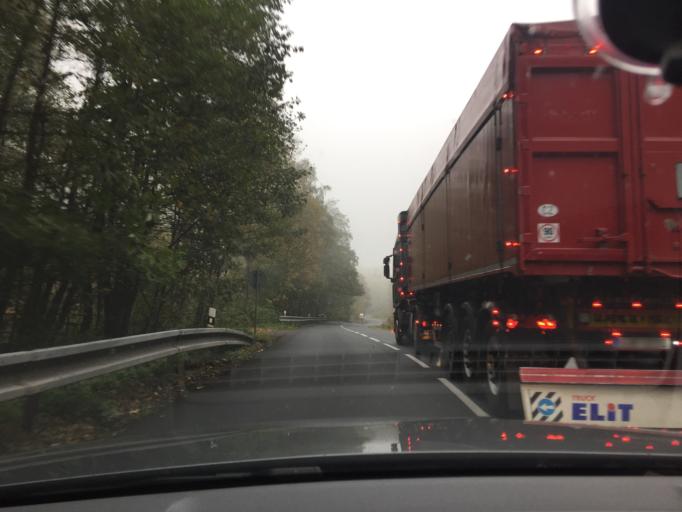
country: CZ
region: Ustecky
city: Libouchec
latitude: 50.7762
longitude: 14.0359
